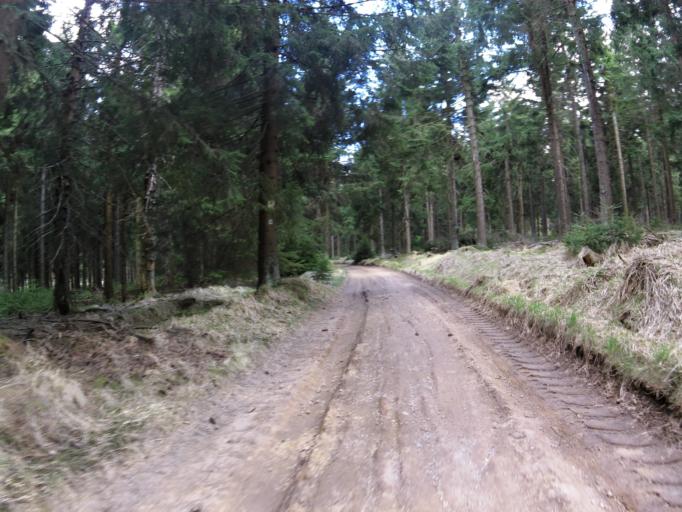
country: DE
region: Thuringia
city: Bermbach
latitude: 50.7132
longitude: 10.6550
